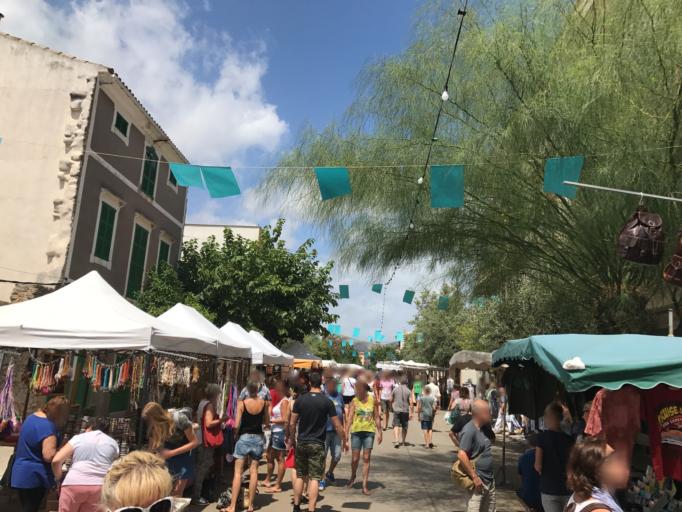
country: ES
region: Balearic Islands
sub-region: Illes Balears
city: Arta
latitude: 39.6922
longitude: 3.3489
